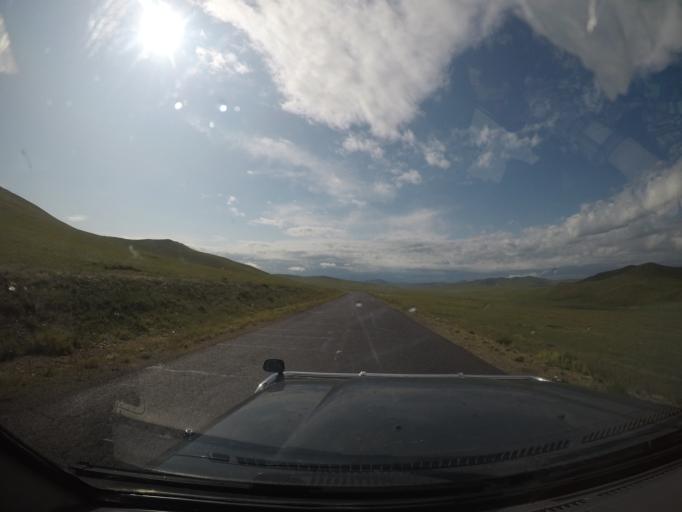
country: MN
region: Hentiy
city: Modot
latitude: 47.8083
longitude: 108.8062
